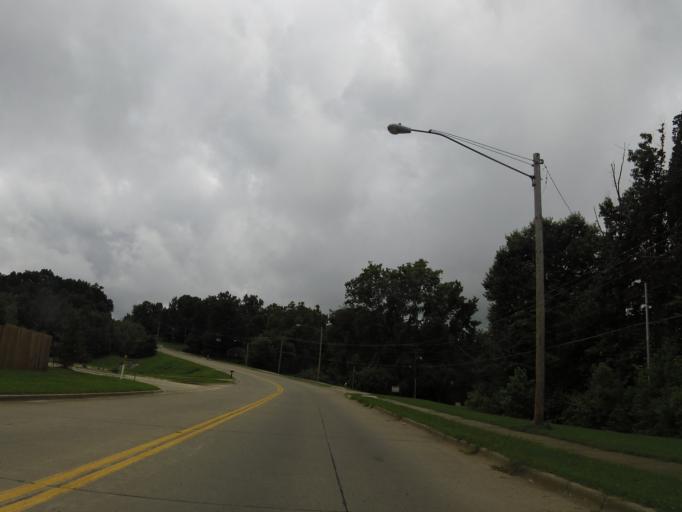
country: US
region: Missouri
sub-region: Cape Girardeau County
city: Cape Girardeau
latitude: 37.3479
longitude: -89.5592
